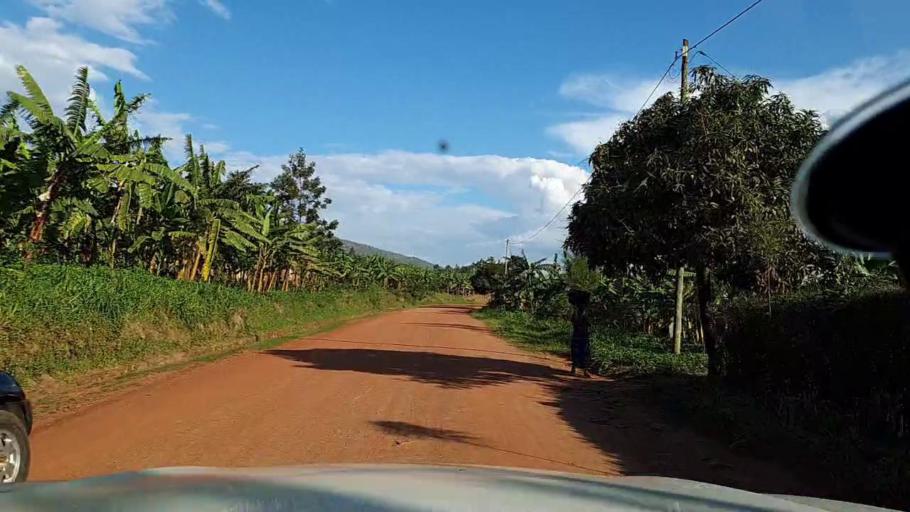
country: RW
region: Kigali
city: Kigali
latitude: -1.8599
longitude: 29.9174
